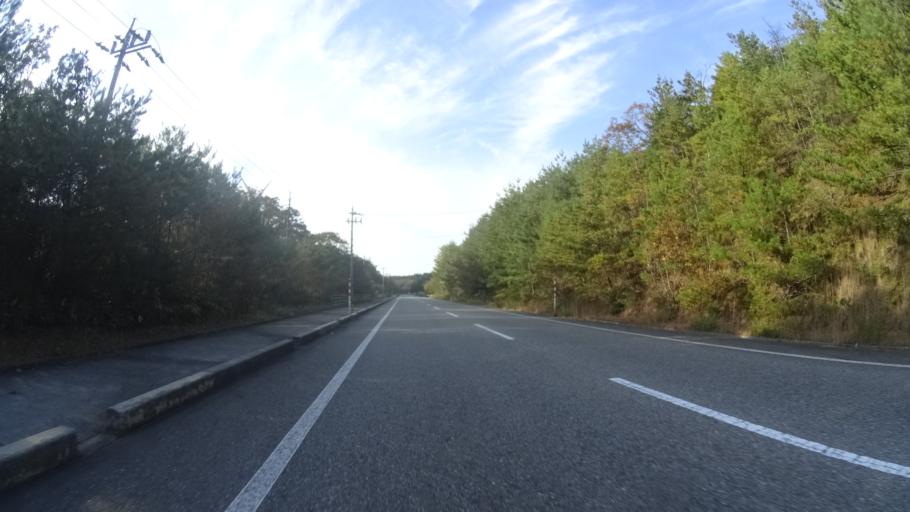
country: JP
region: Ishikawa
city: Hakui
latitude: 37.0720
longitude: 136.7351
